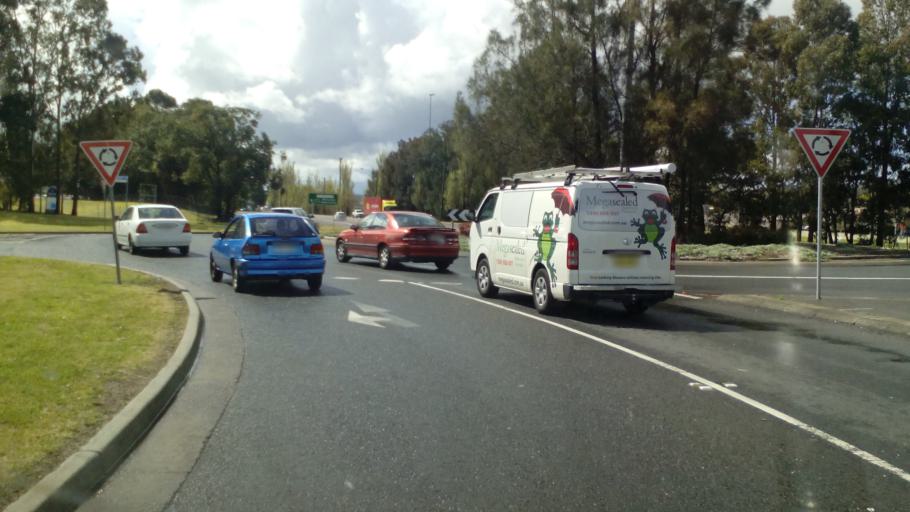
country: AU
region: New South Wales
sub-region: Lake Macquarie Shire
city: Glendale
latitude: -32.9576
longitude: 151.6169
